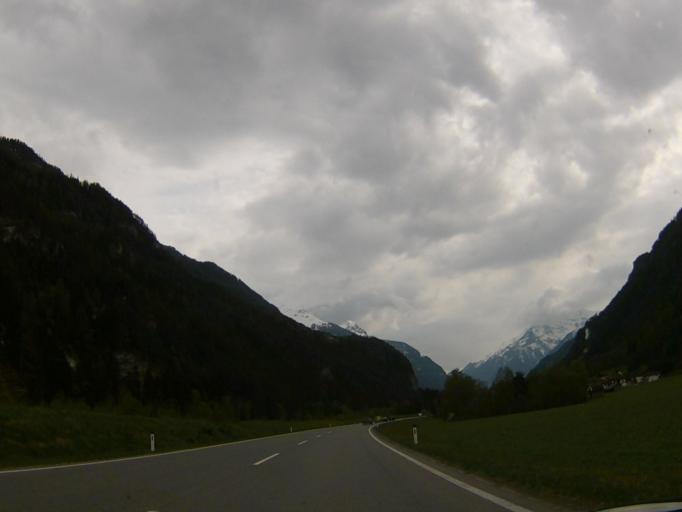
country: AT
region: Tyrol
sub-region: Politischer Bezirk Landeck
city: Serfaus
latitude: 47.0070
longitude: 10.5980
